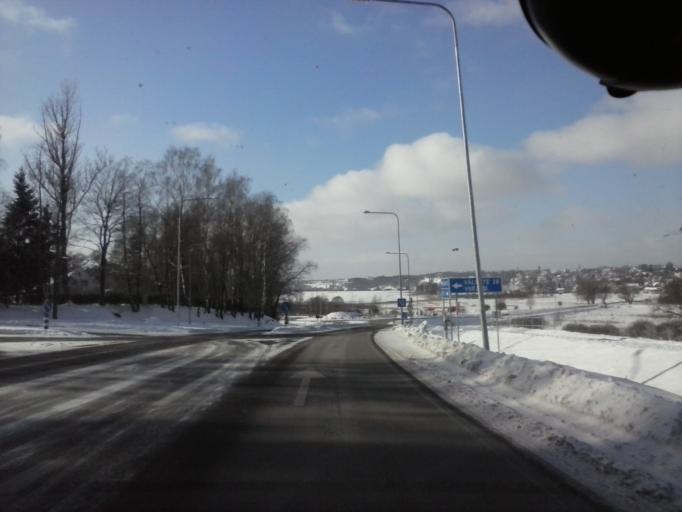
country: EE
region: Viljandimaa
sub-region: Viiratsi vald
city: Viiratsi
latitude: 58.3634
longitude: 25.6396
